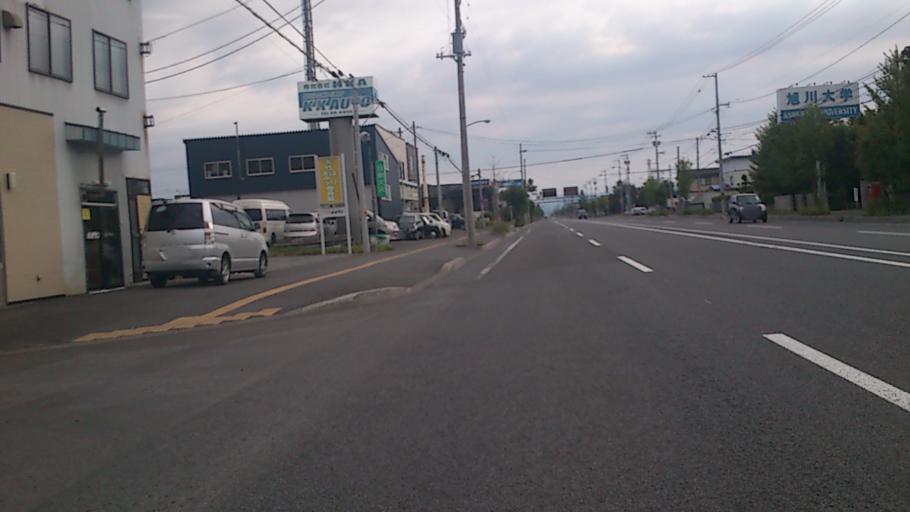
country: JP
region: Hokkaido
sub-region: Asahikawa-shi
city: Asahikawa
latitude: 43.8171
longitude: 142.4443
